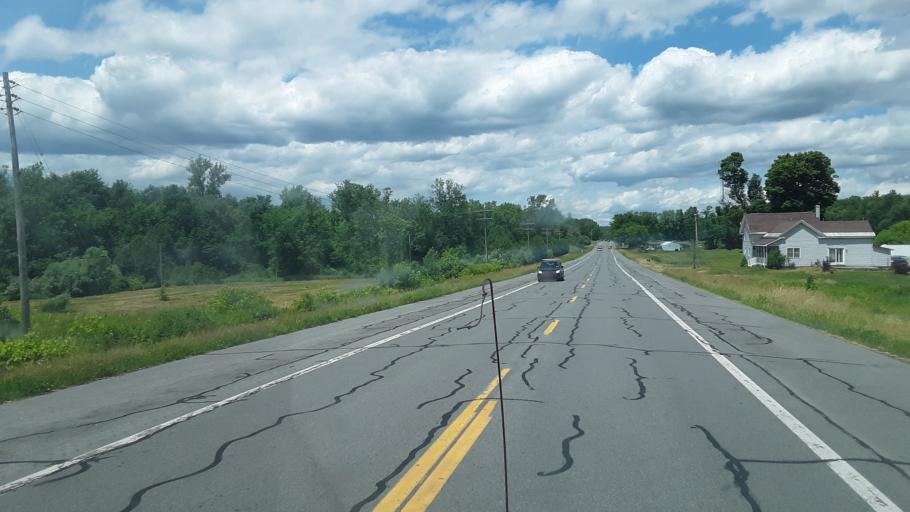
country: US
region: New York
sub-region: Oneida County
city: Rome
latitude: 43.2125
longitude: -75.5899
